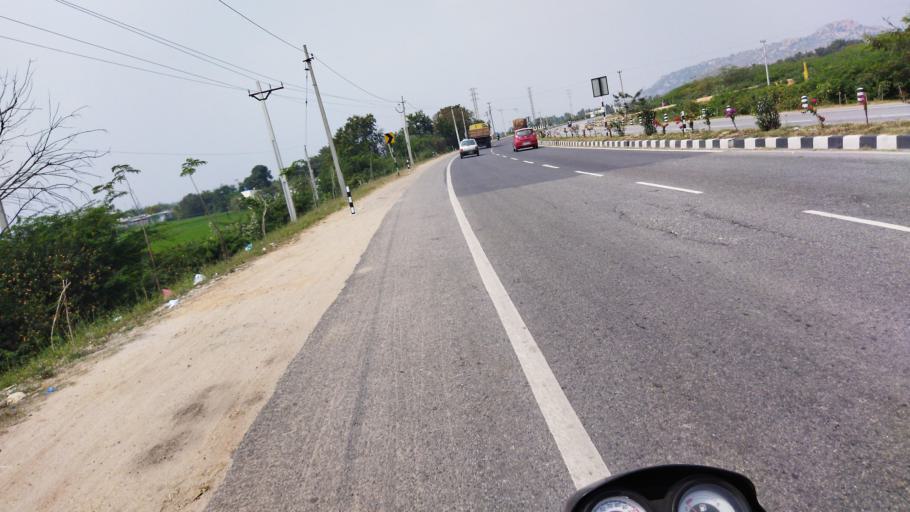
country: IN
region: Telangana
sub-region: Nalgonda
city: Nalgonda
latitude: 17.0792
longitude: 79.2787
